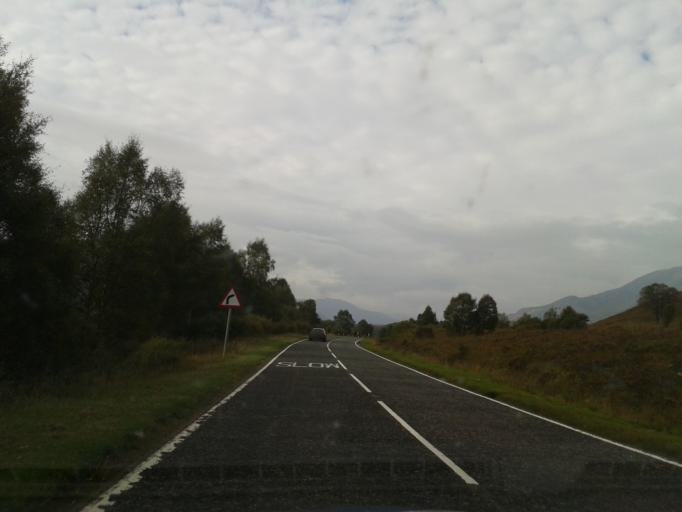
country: GB
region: Scotland
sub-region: Highland
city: Spean Bridge
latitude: 57.1454
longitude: -4.9646
